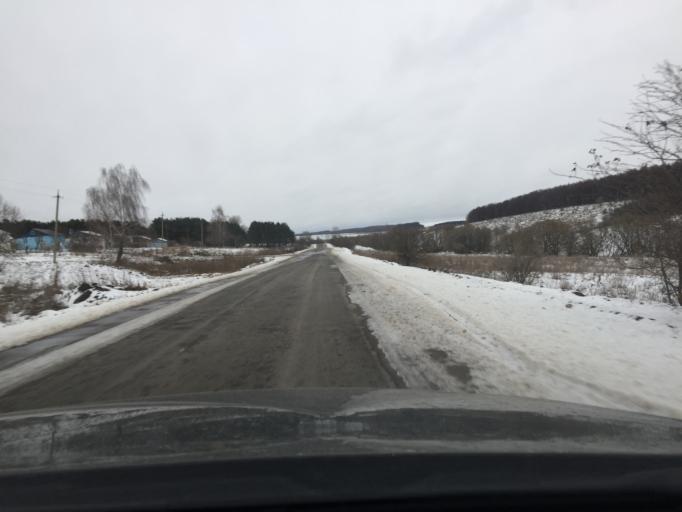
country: RU
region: Tula
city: Shchekino
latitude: 53.8262
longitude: 37.5589
